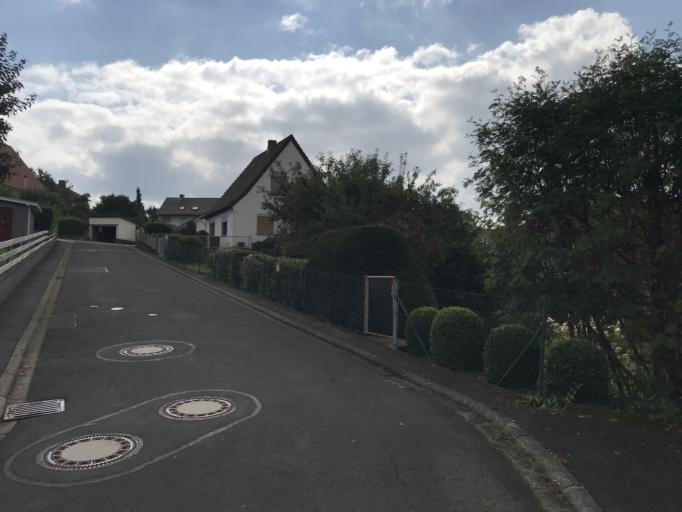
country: DE
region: Hesse
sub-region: Regierungsbezirk Giessen
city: Lauterbach
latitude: 50.6337
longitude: 9.3883
